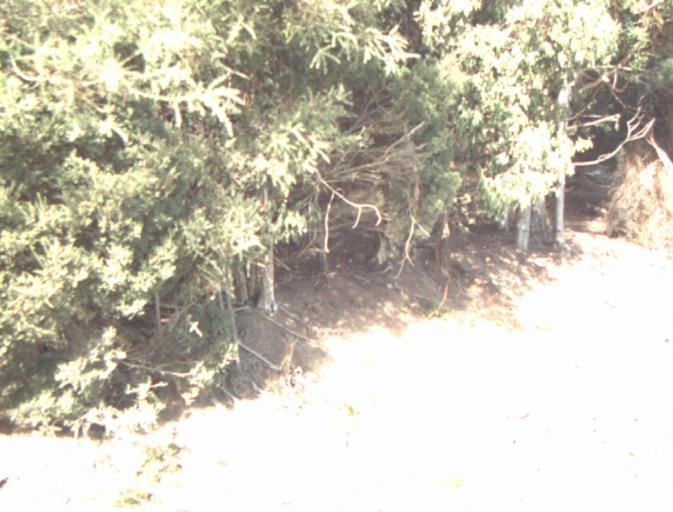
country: AU
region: Tasmania
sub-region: Launceston
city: Mayfield
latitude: -41.2620
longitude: 147.2242
